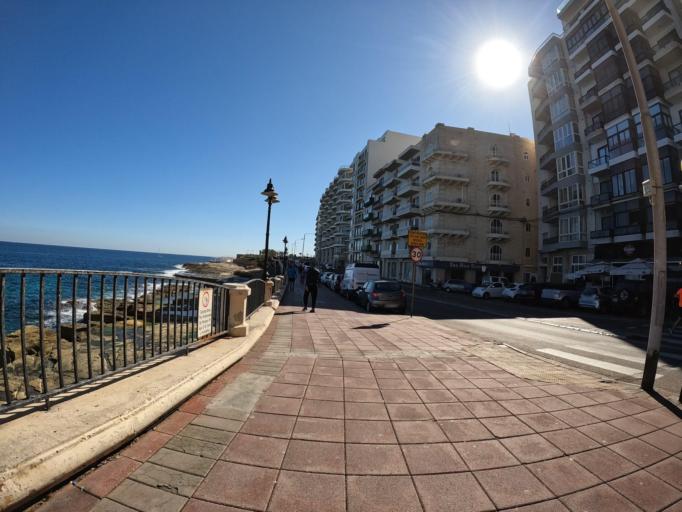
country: MT
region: Tas-Sliema
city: Sliema
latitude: 35.9116
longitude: 14.5072
